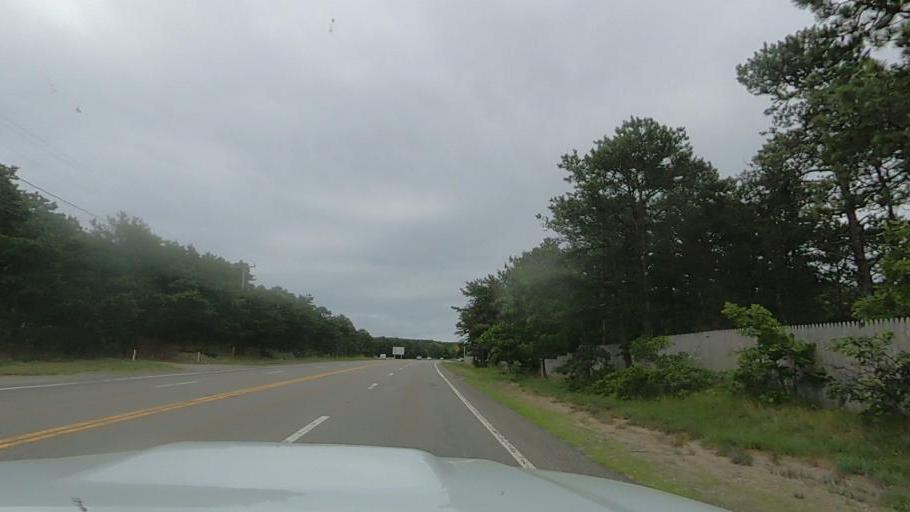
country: US
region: Massachusetts
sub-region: Barnstable County
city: Truro
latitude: 42.0460
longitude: -70.0982
